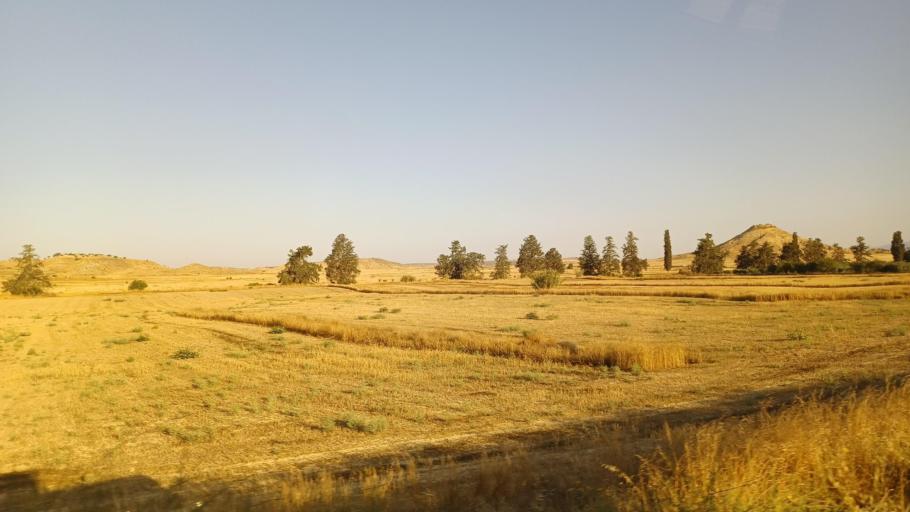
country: CY
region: Larnaka
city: Athienou
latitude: 35.0532
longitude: 33.4996
